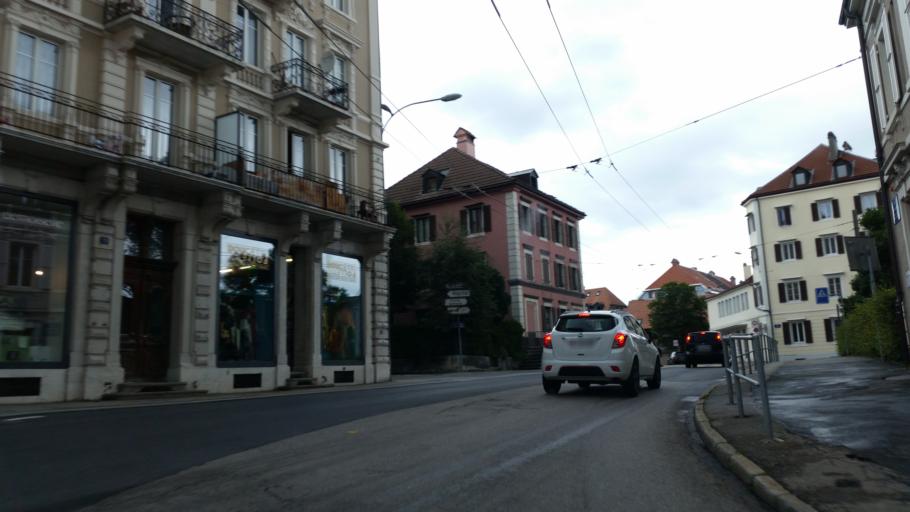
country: CH
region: Neuchatel
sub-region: La Chaux-de-Fonds District
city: La Chaux-de-Fonds
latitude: 47.1064
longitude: 6.8305
